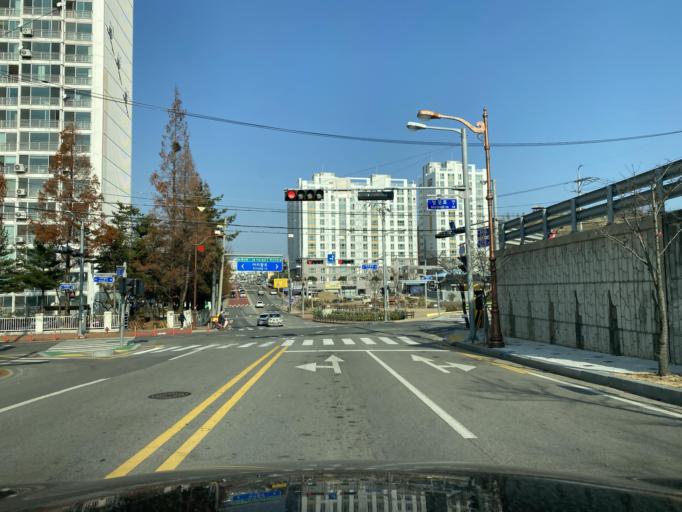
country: KR
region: Chungcheongnam-do
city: Yesan
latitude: 36.6862
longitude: 126.8361
